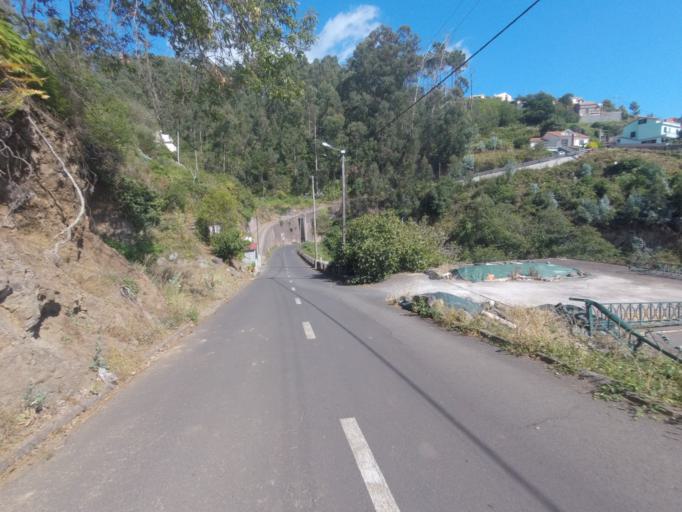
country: PT
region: Madeira
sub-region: Ribeira Brava
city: Campanario
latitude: 32.6916
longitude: -17.0312
